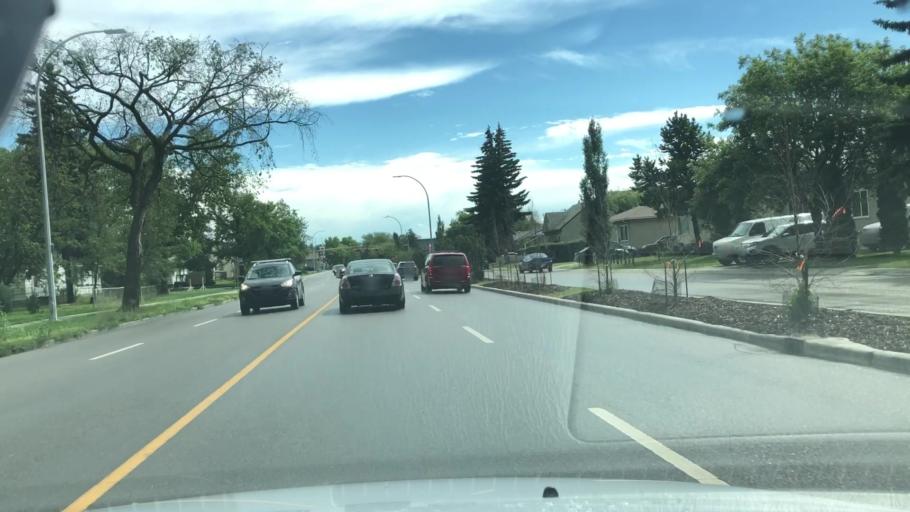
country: CA
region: Alberta
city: Edmonton
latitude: 53.5728
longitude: -113.5413
